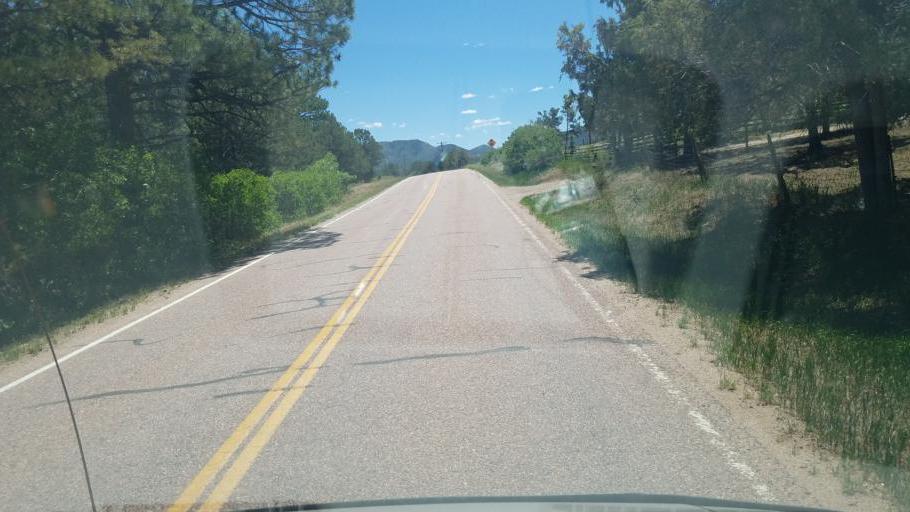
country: US
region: Colorado
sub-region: Custer County
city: Westcliffe
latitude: 38.3099
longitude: -105.6228
